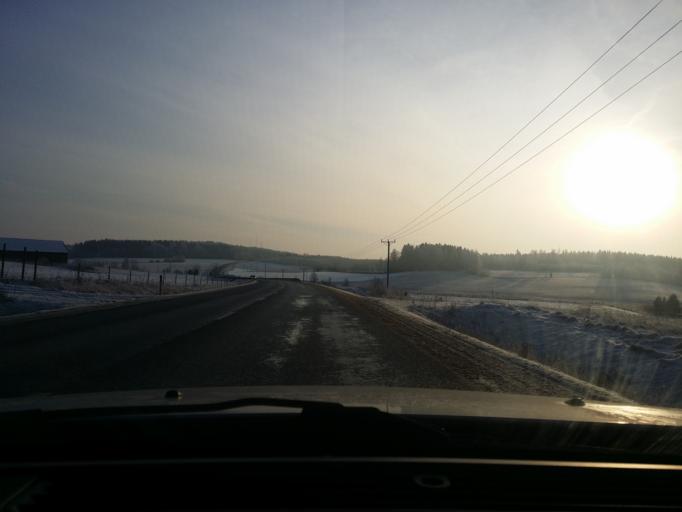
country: SE
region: OErebro
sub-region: Lindesbergs Kommun
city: Lindesberg
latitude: 59.5902
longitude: 15.1870
